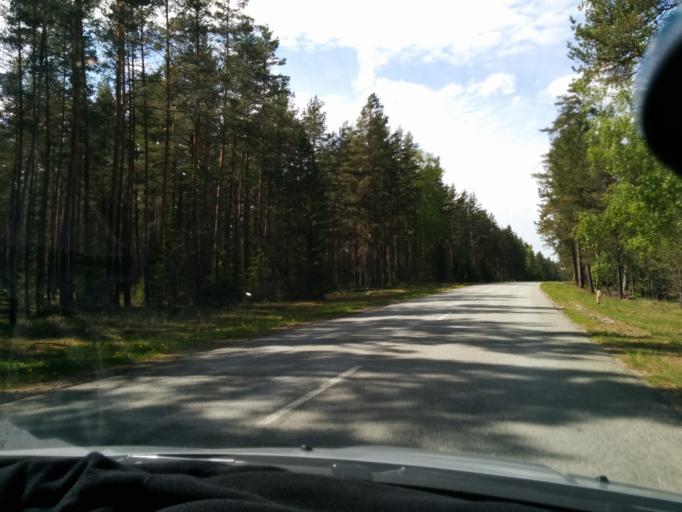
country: EE
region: Laeaene-Virumaa
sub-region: Kadrina vald
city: Kadrina
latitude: 59.5543
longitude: 26.0041
